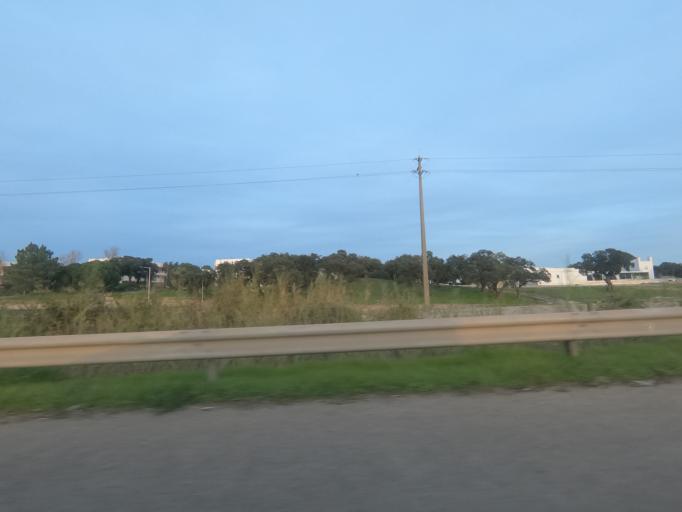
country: PT
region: Setubal
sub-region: Setubal
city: Setubal
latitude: 38.5199
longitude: -8.8406
